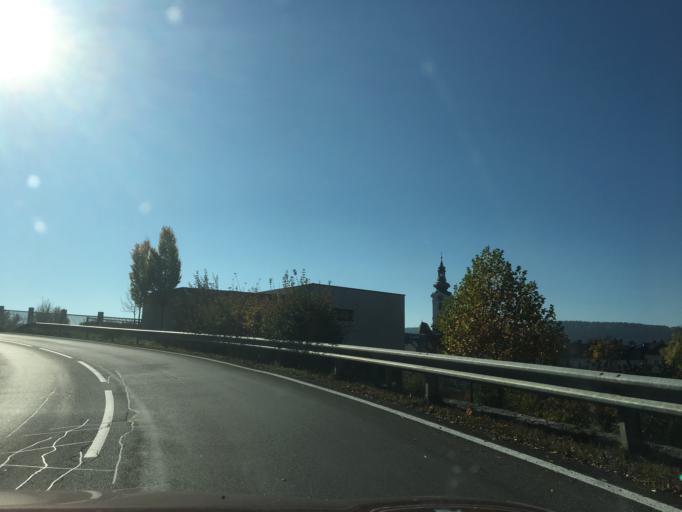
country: AT
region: Upper Austria
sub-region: Politischer Bezirk Freistadt
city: Freistadt
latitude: 48.5118
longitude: 14.5087
